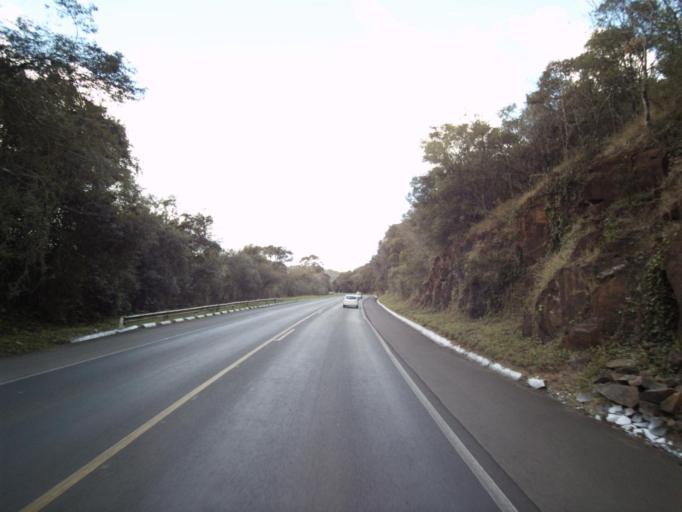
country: BR
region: Santa Catarina
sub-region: Campos Novos
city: Campos Novos
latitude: -27.3090
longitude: -51.3752
